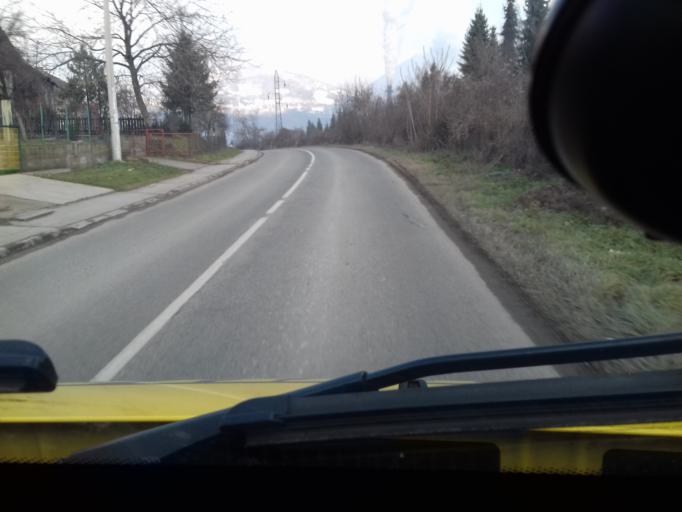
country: BA
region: Federation of Bosnia and Herzegovina
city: Zenica
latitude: 44.2251
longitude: 17.8918
